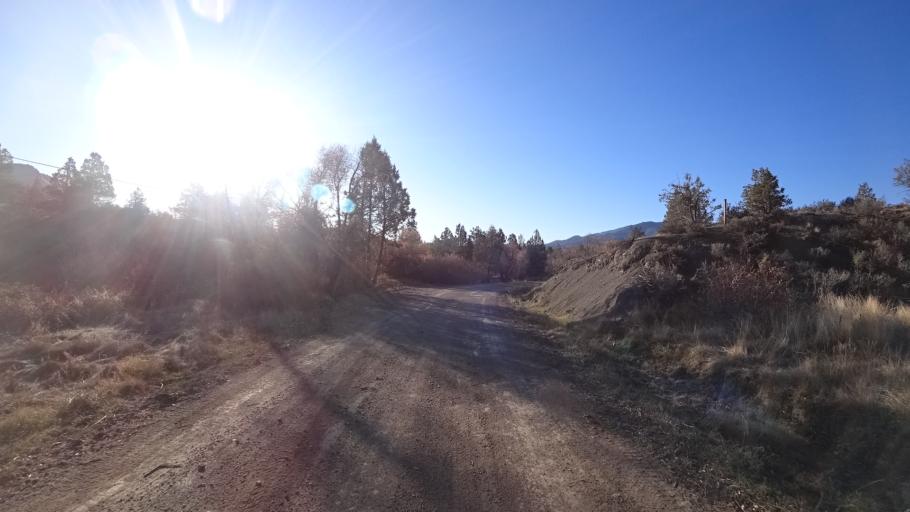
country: US
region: Oregon
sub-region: Jackson County
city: Ashland
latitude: 41.9920
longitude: -122.6235
